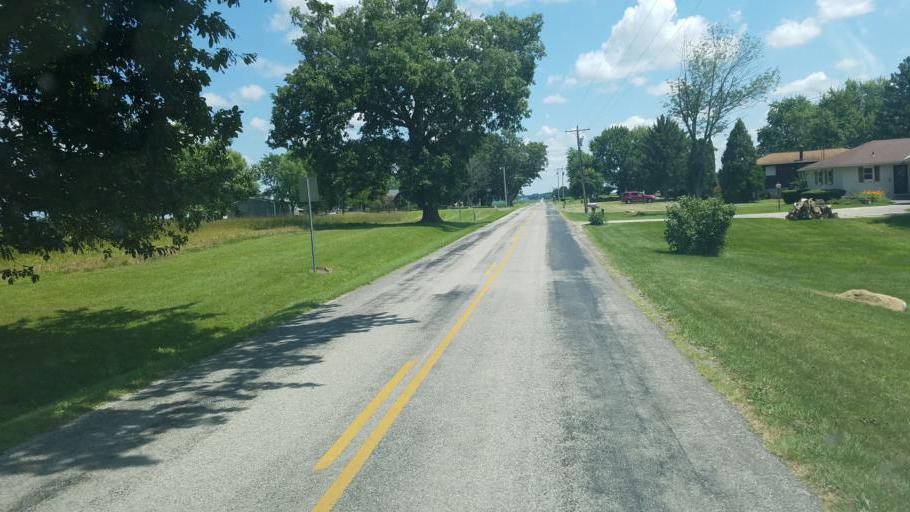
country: US
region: Ohio
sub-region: Marion County
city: Marion
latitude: 40.6587
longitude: -83.1718
